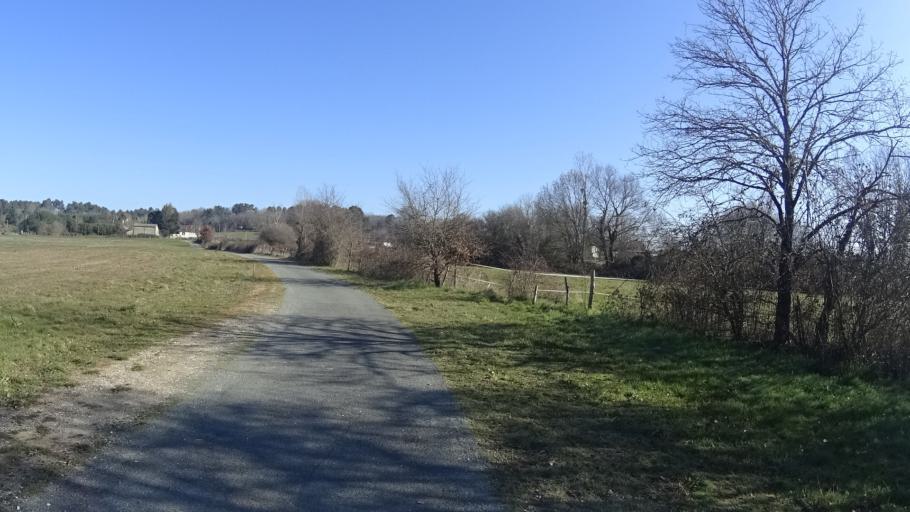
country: FR
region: Aquitaine
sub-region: Departement de la Dordogne
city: Montpon-Menesterol
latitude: 45.0320
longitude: 0.2242
